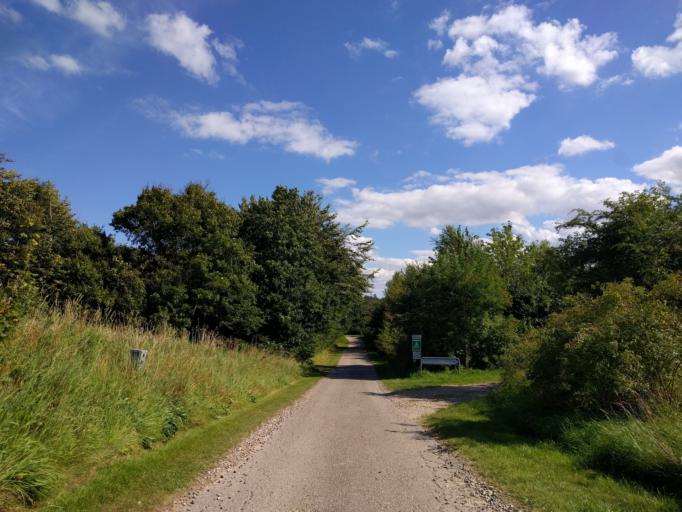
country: DK
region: Central Jutland
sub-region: Viborg Kommune
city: Bjerringbro
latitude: 56.5230
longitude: 9.5915
